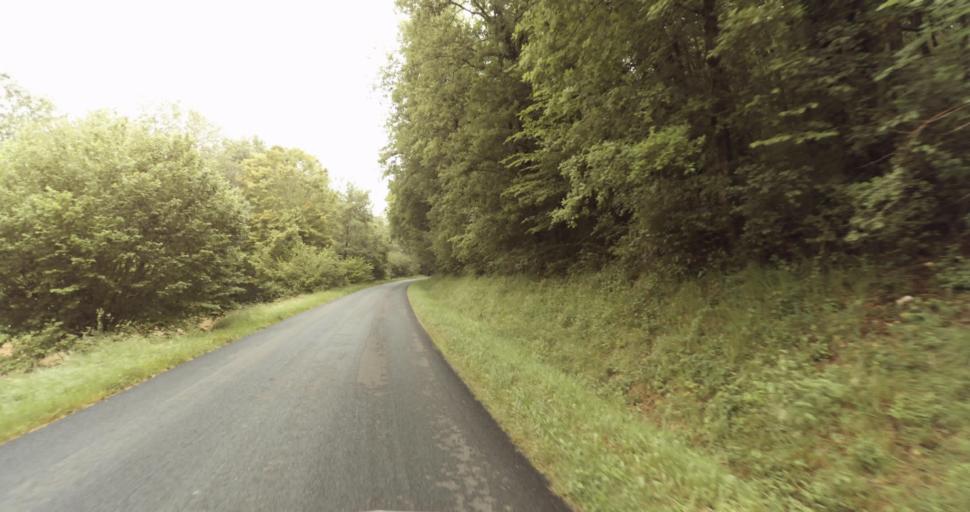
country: FR
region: Aquitaine
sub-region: Departement de la Dordogne
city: Lalinde
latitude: 44.8641
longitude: 0.7737
